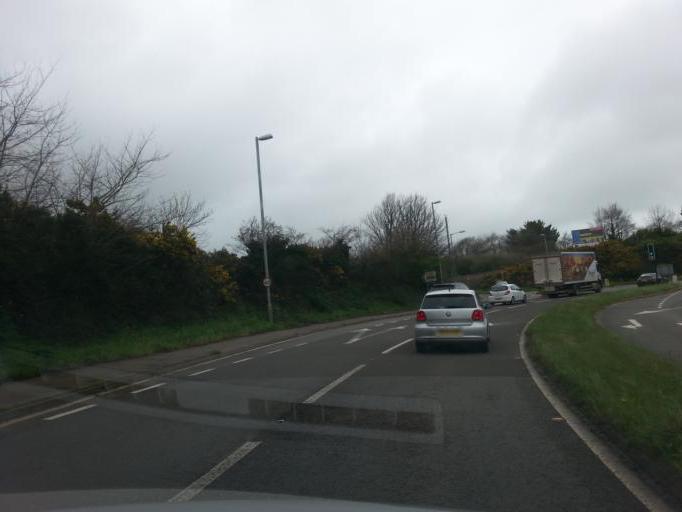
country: GB
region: England
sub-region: Cornwall
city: Camborne
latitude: 50.2298
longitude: -5.2838
